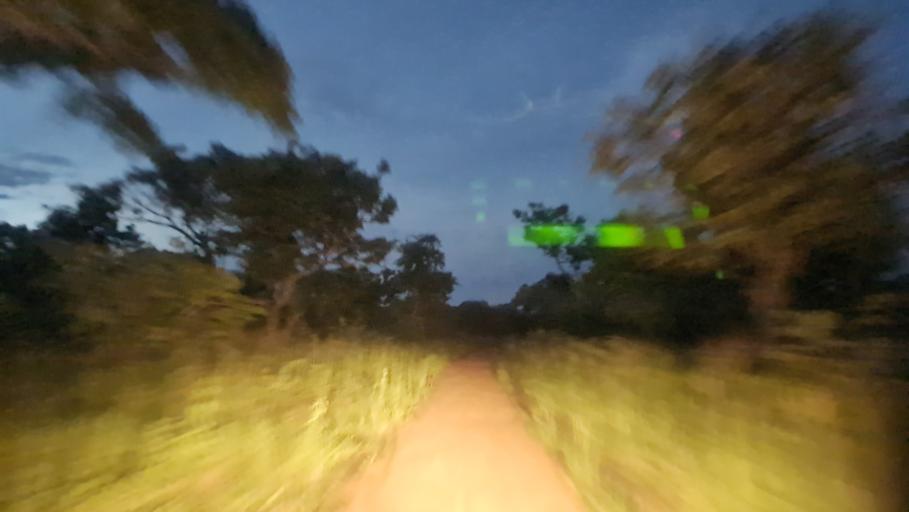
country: MZ
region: Nampula
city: Nampula
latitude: -14.6774
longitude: 39.8313
